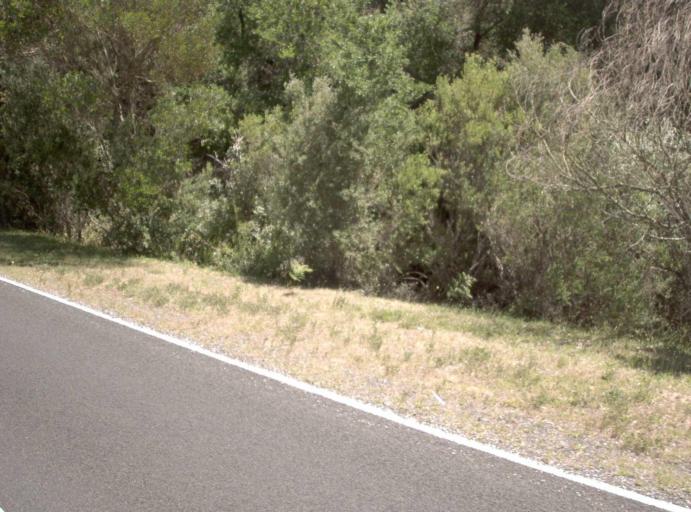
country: AU
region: Victoria
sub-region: Latrobe
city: Morwell
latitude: -38.8840
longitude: 146.2584
